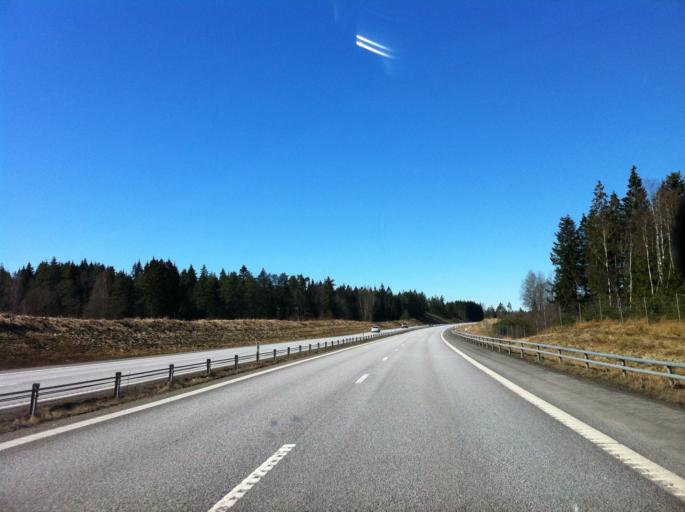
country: SE
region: Vaestra Goetaland
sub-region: Vanersborgs Kommun
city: Vanersborg
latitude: 58.3669
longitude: 12.3531
